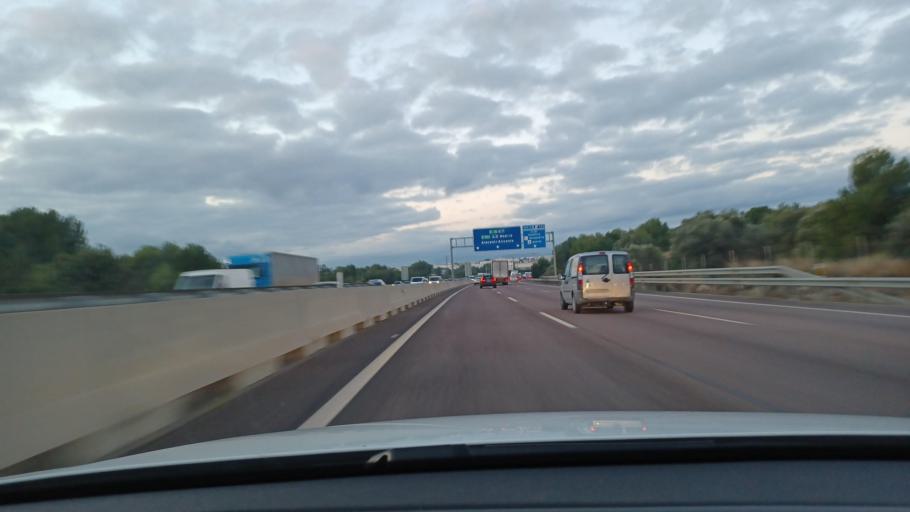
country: ES
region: Valencia
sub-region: Provincia de Valencia
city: Manises
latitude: 39.5307
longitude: -0.4629
